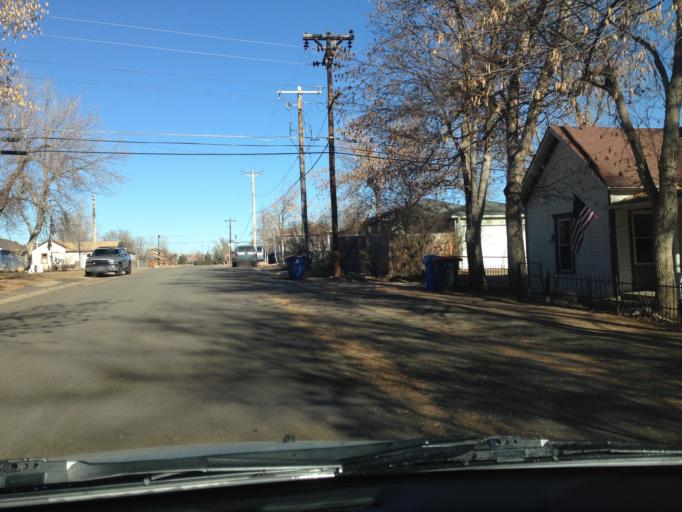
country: US
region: Colorado
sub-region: Boulder County
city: Superior
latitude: 39.9523
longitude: -105.1694
